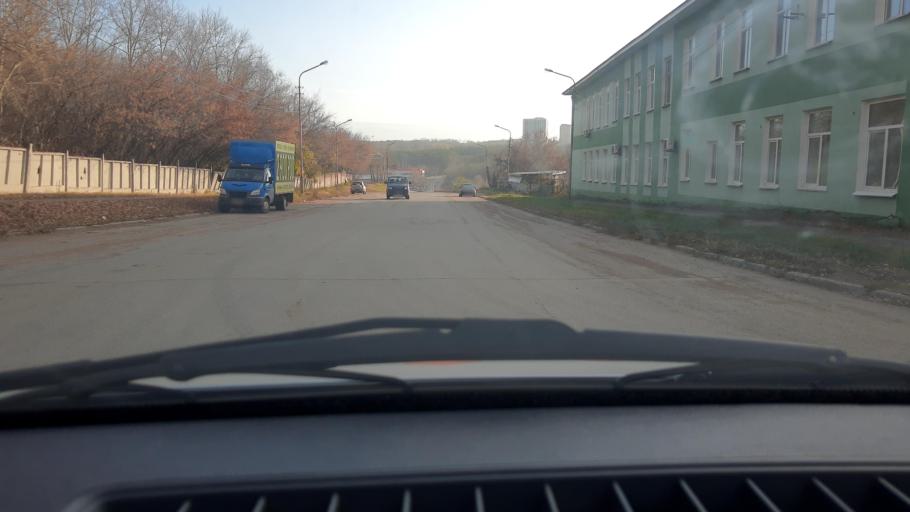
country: RU
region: Bashkortostan
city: Ufa
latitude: 54.7293
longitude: 55.9908
